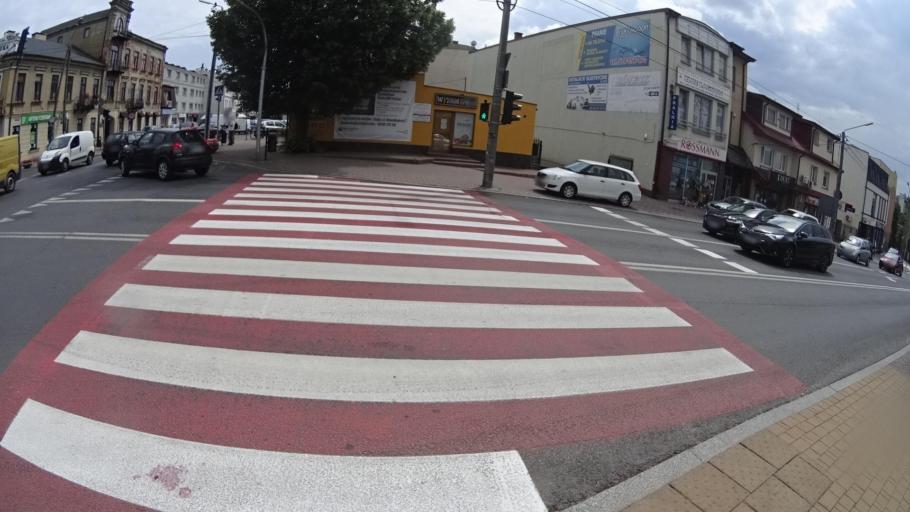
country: PL
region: Masovian Voivodeship
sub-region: Powiat grojecki
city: Grojec
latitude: 51.8656
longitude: 20.8662
